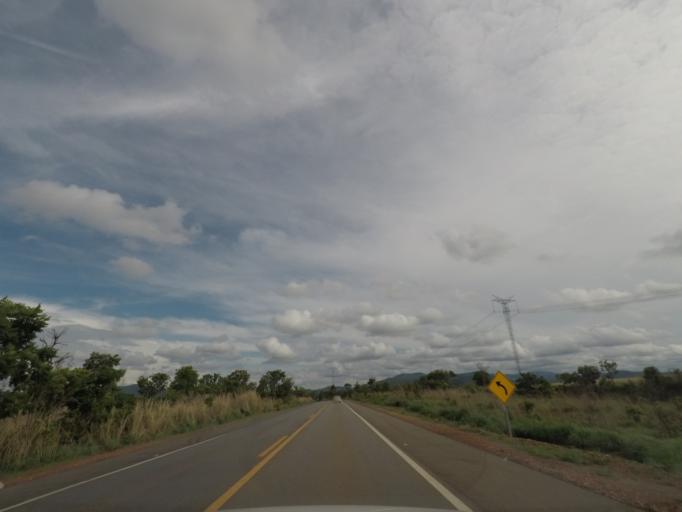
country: BR
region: Goias
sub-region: Barro Alto
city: Barro Alto
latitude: -14.8638
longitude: -49.0179
